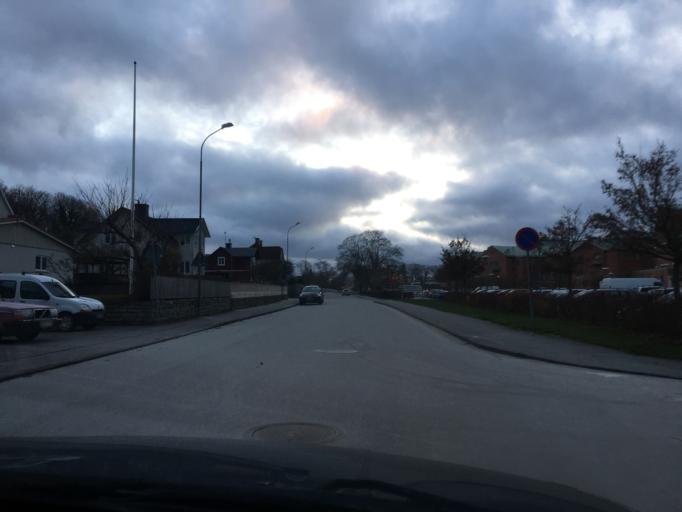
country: SE
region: Gotland
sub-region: Gotland
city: Visby
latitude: 57.6495
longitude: 18.3031
